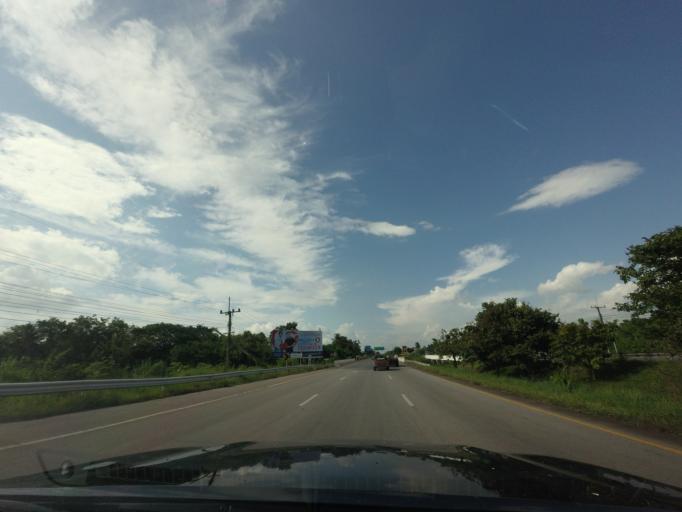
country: TH
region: Nong Khai
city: Sa Khrai
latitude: 17.6819
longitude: 102.7845
